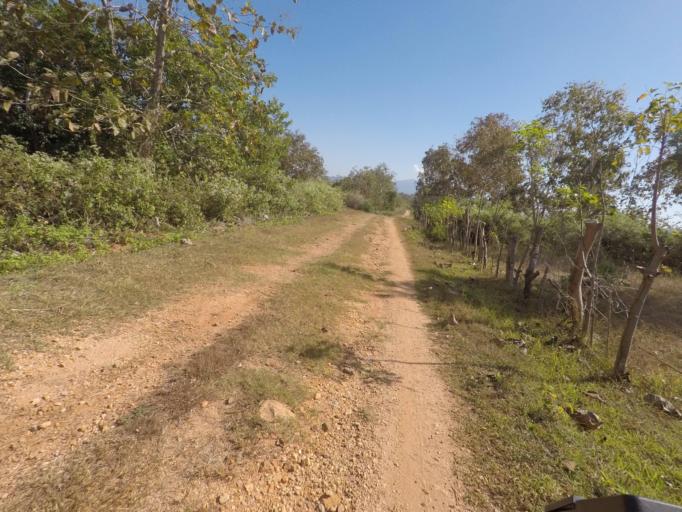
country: TL
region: Bobonaro
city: Maliana
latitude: -8.9505
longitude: 125.2153
